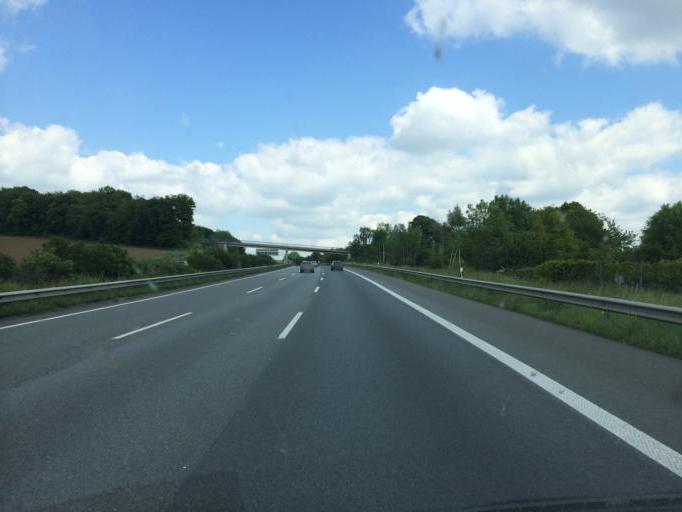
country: DE
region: North Rhine-Westphalia
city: Bad Oeynhausen
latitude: 52.1443
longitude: 8.7880
